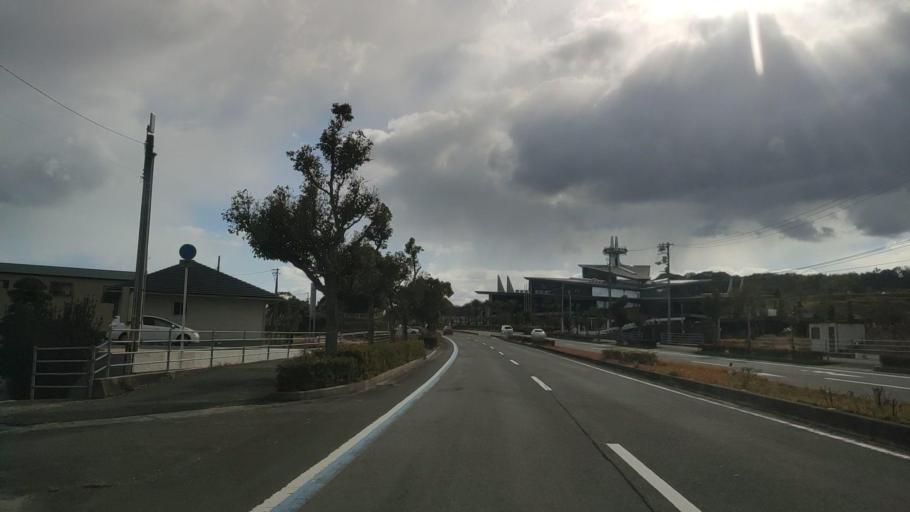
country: JP
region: Ehime
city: Hojo
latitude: 34.0651
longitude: 132.9521
